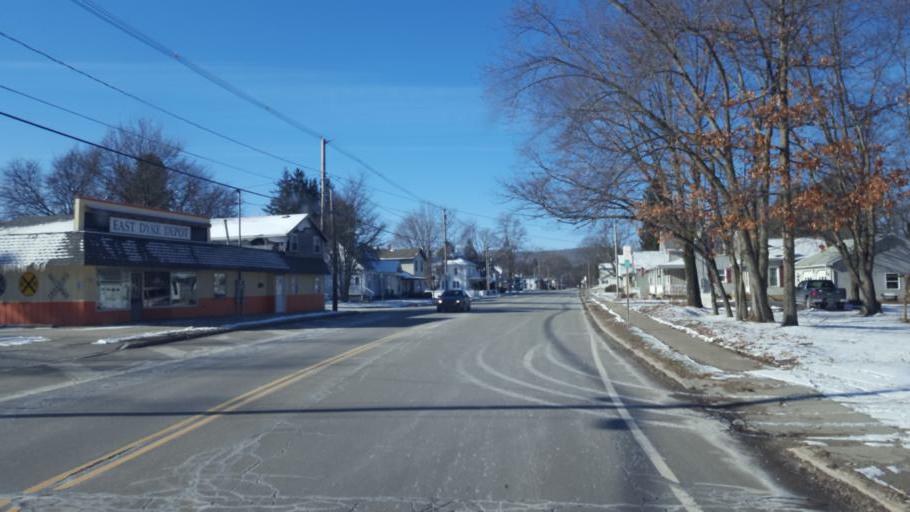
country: US
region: New York
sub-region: Allegany County
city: Wellsville
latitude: 42.1217
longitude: -77.9295
